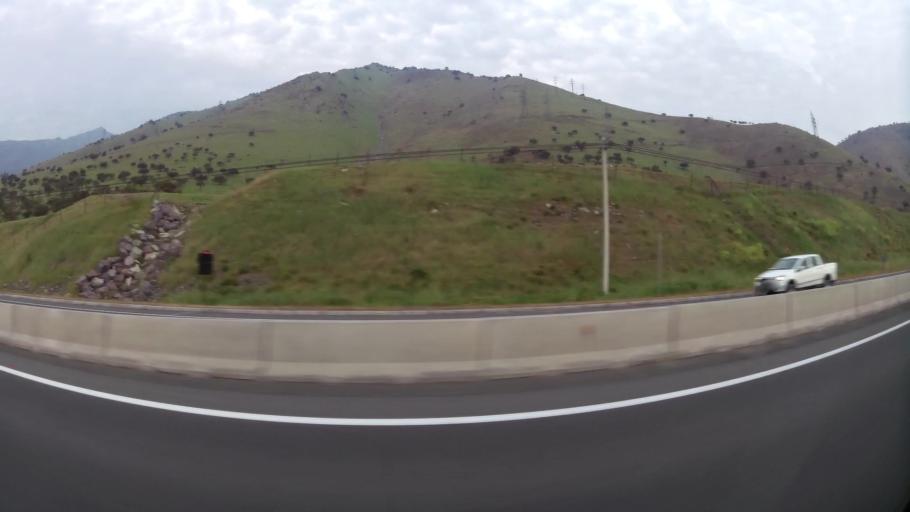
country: CL
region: Santiago Metropolitan
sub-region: Provincia de Chacabuco
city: Chicureo Abajo
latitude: -33.3605
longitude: -70.6172
